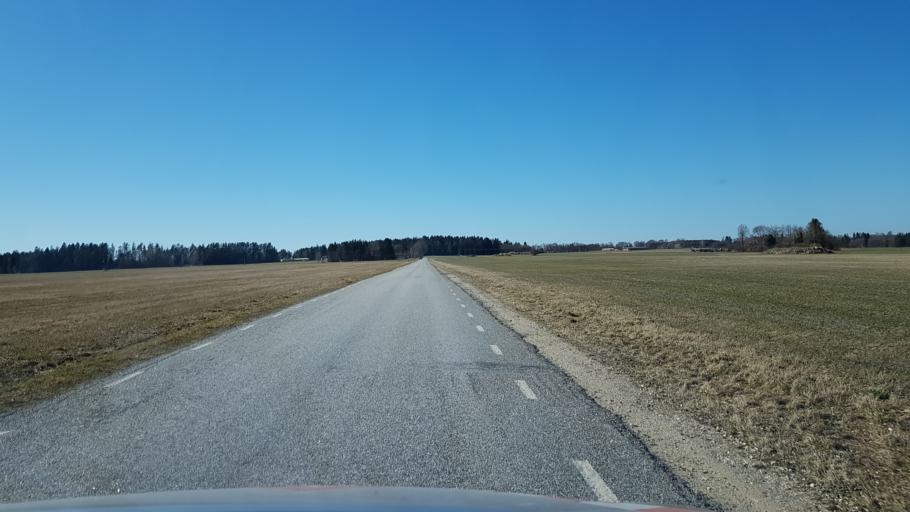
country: EE
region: Laeaene-Virumaa
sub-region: Viru-Nigula vald
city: Kunda
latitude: 59.4030
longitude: 26.5443
